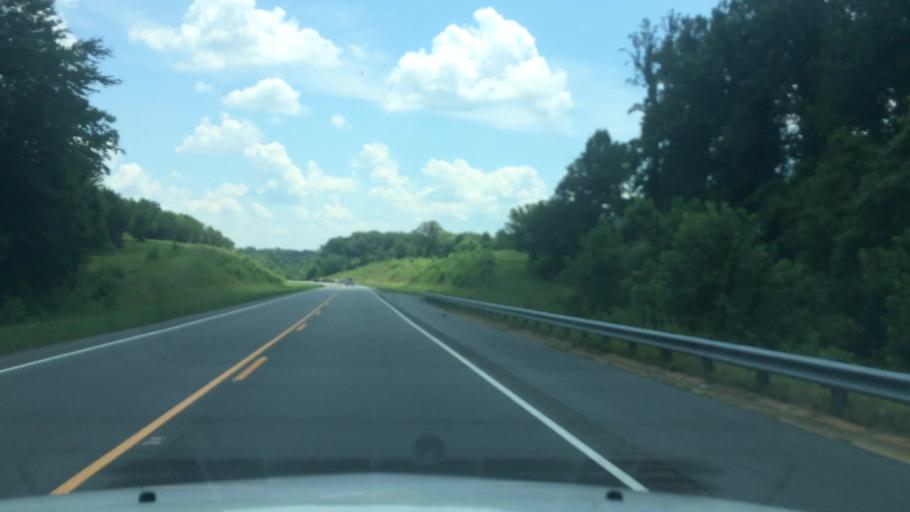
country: US
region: North Carolina
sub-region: Alexander County
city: Stony Point
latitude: 35.8675
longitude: -81.0625
